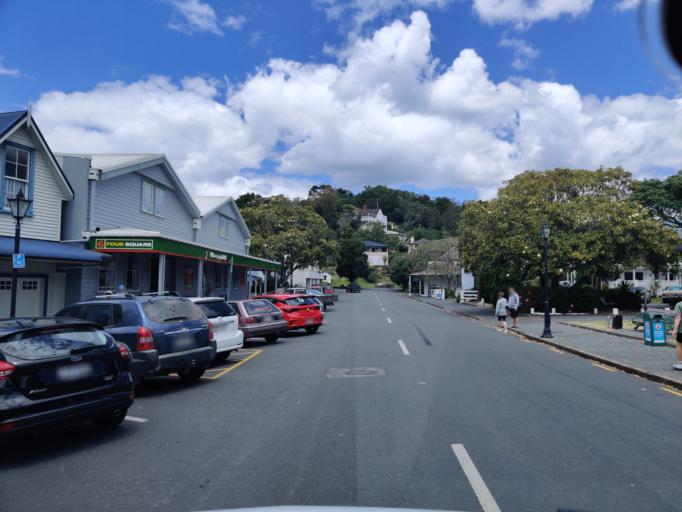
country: NZ
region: Northland
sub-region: Far North District
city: Paihia
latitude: -35.2624
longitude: 174.1224
